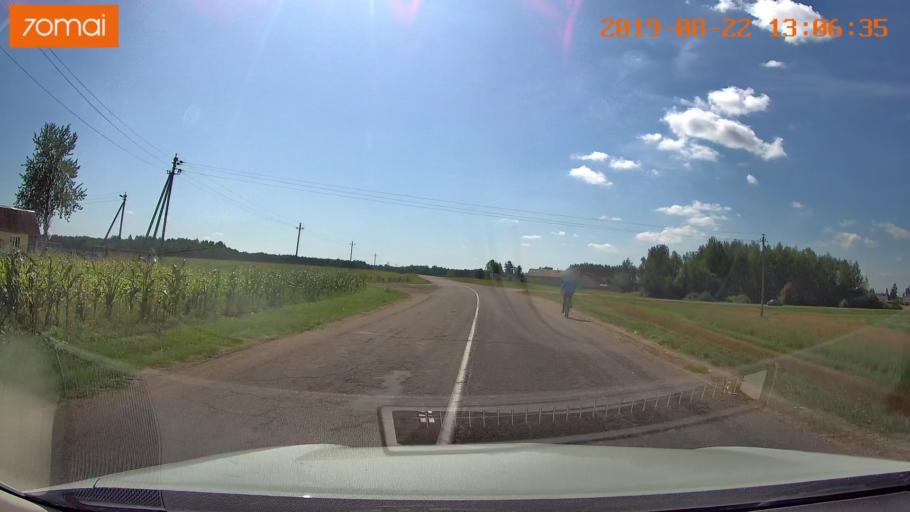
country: BY
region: Minsk
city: Prawdzinski
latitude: 53.3454
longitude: 27.8374
